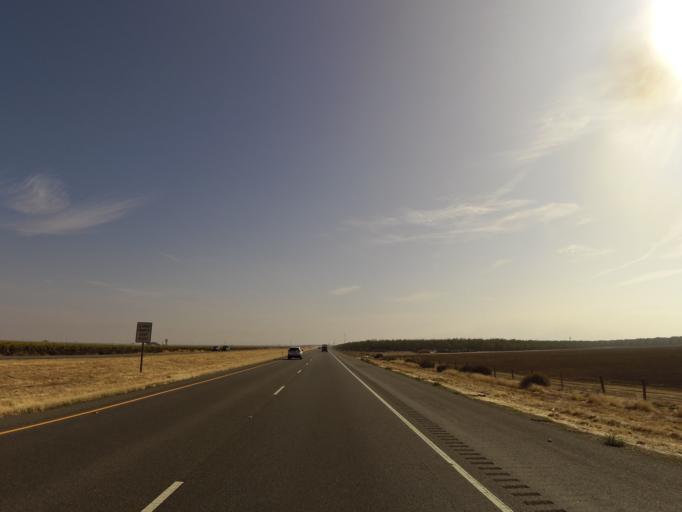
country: US
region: California
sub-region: Kern County
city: Greenfield
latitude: 35.0882
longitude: -119.0304
